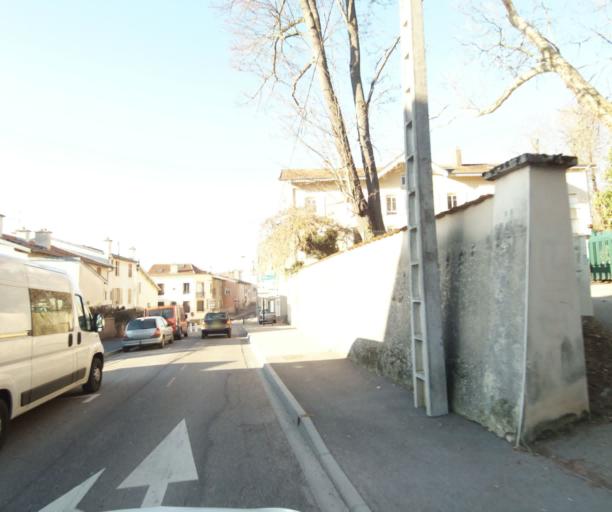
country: FR
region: Lorraine
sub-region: Departement de Meurthe-et-Moselle
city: Malzeville
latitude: 48.7091
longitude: 6.1876
